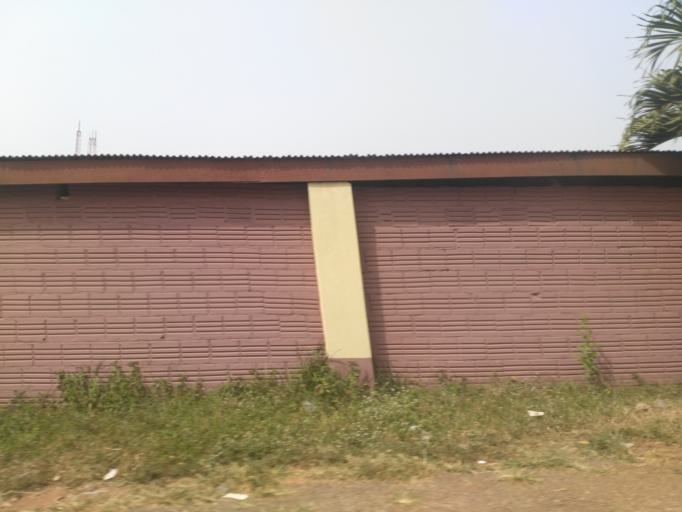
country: GH
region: Ashanti
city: Kumasi
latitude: 6.6806
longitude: -1.6067
